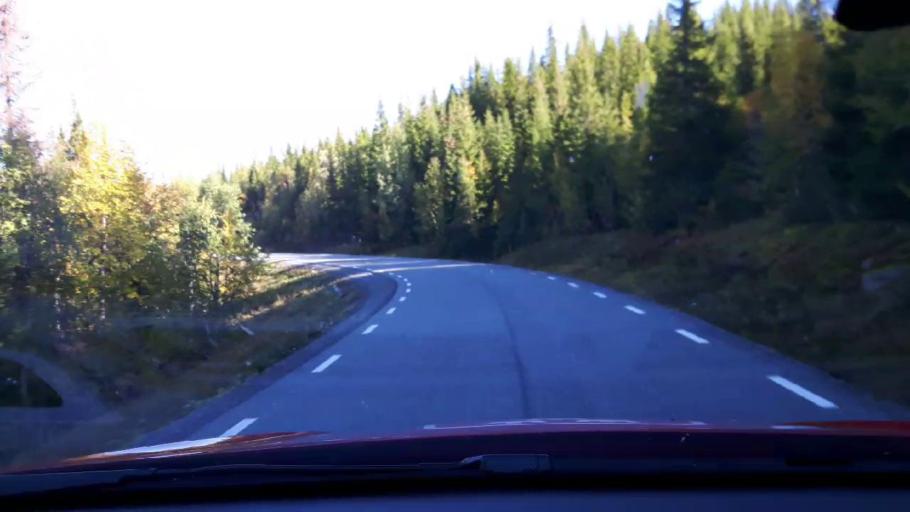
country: NO
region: Nord-Trondelag
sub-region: Lierne
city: Sandvika
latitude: 64.6109
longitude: 13.7013
